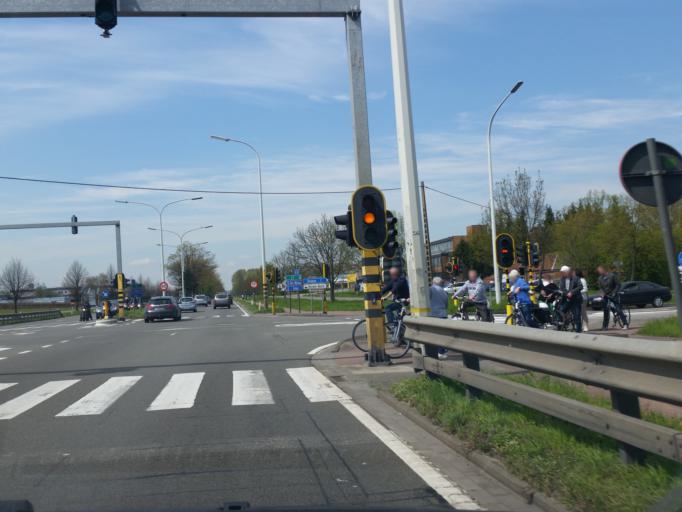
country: BE
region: Flanders
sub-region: Provincie Antwerpen
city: Bornem
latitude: 51.0921
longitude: 4.2680
